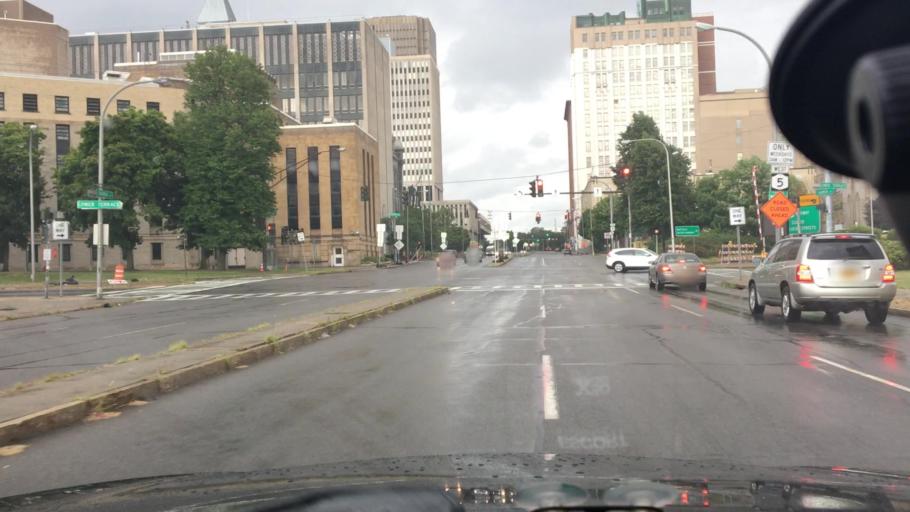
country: US
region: New York
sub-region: Erie County
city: Buffalo
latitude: 42.8840
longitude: -78.8806
